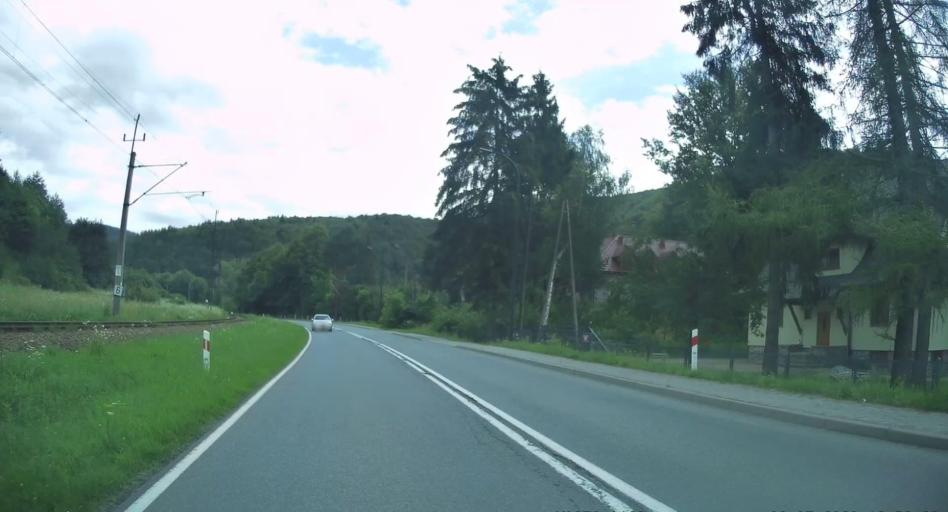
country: PL
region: Lesser Poland Voivodeship
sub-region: Powiat nowosadecki
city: Piwniczna-Zdroj
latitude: 49.3619
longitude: 20.7851
